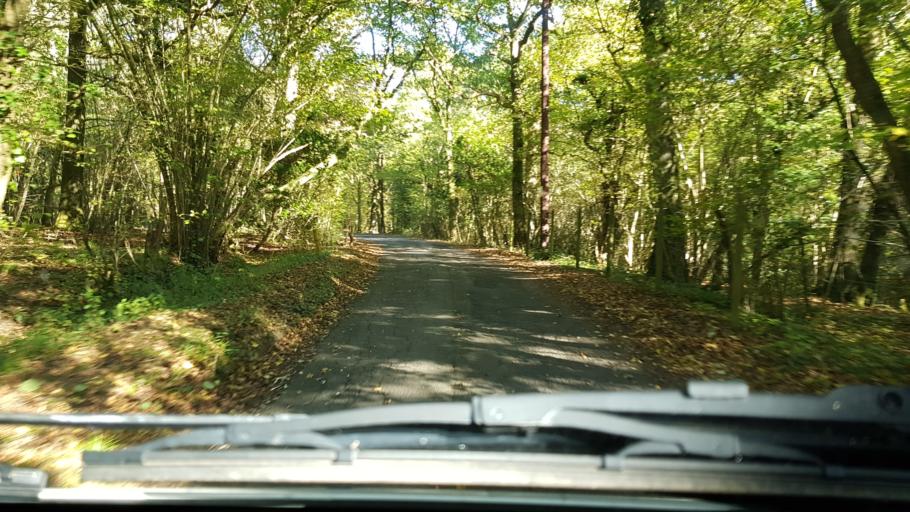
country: GB
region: England
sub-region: Surrey
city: Ockley
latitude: 51.1337
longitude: -0.3470
